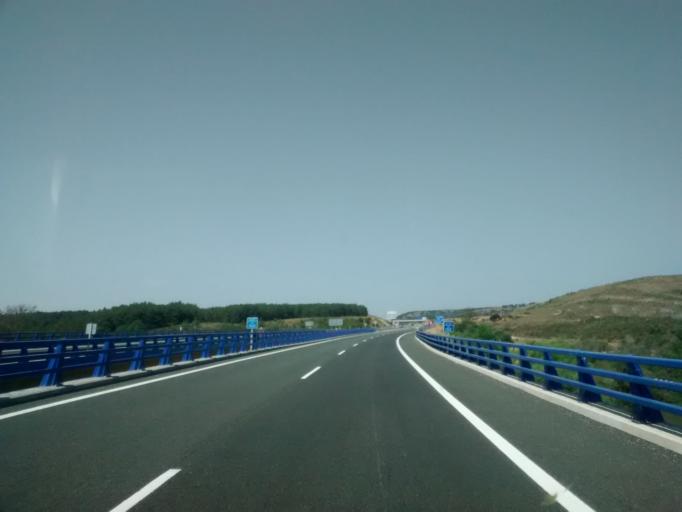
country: ES
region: Castille and Leon
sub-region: Provincia de Palencia
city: Aguilar de Campoo
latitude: 42.7723
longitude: -4.2545
